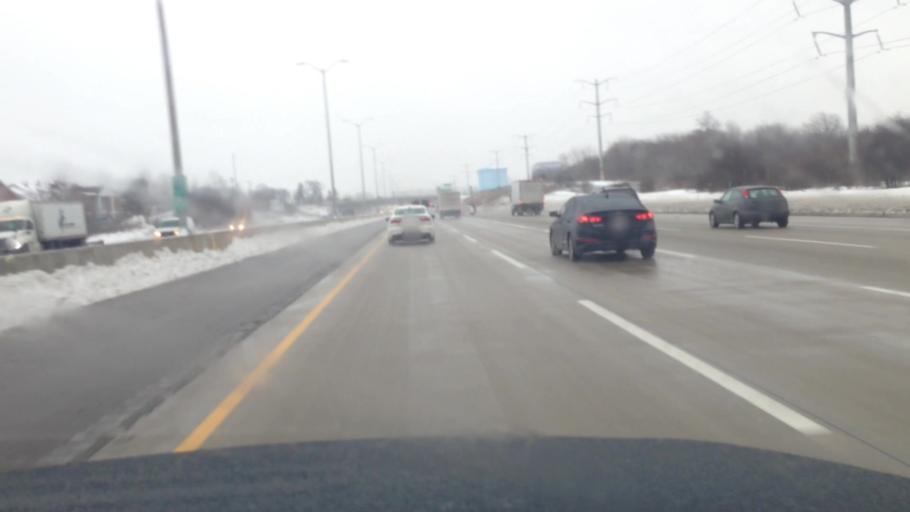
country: US
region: Illinois
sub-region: Cook County
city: Streamwood
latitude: 42.0660
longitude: -88.1683
